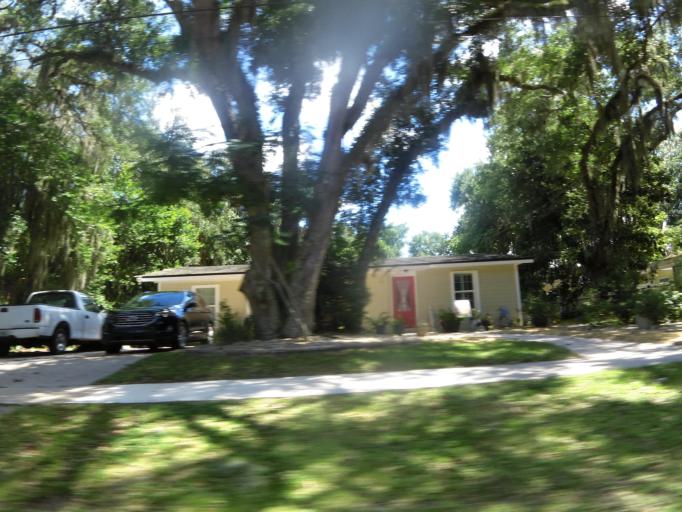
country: US
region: Florida
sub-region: Nassau County
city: Fernandina Beach
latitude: 30.6665
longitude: -81.4446
